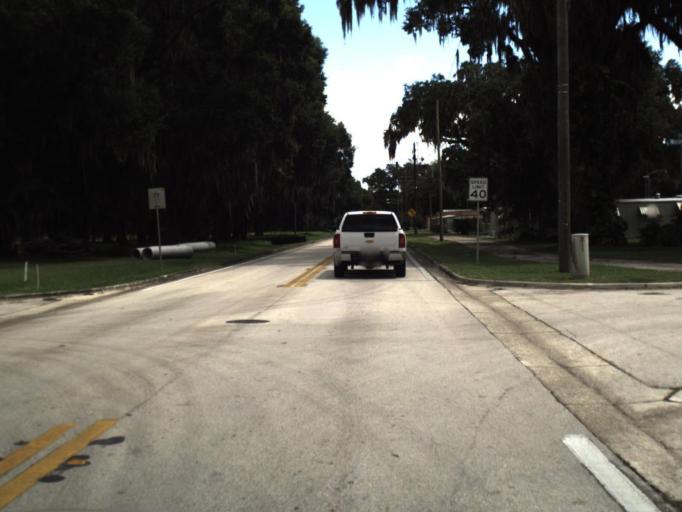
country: US
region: Florida
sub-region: Polk County
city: Fort Meade
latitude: 27.7519
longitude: -81.7870
